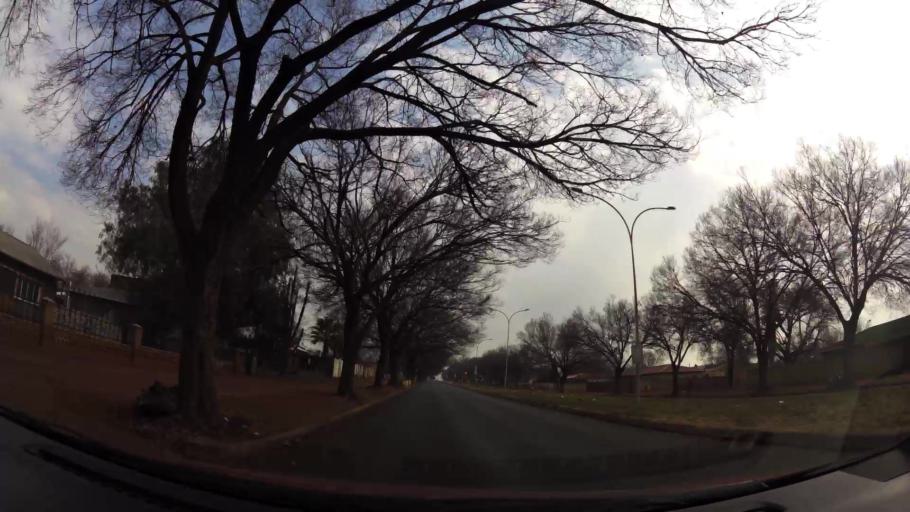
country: ZA
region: Gauteng
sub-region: Sedibeng District Municipality
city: Vanderbijlpark
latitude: -26.6914
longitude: 27.8290
